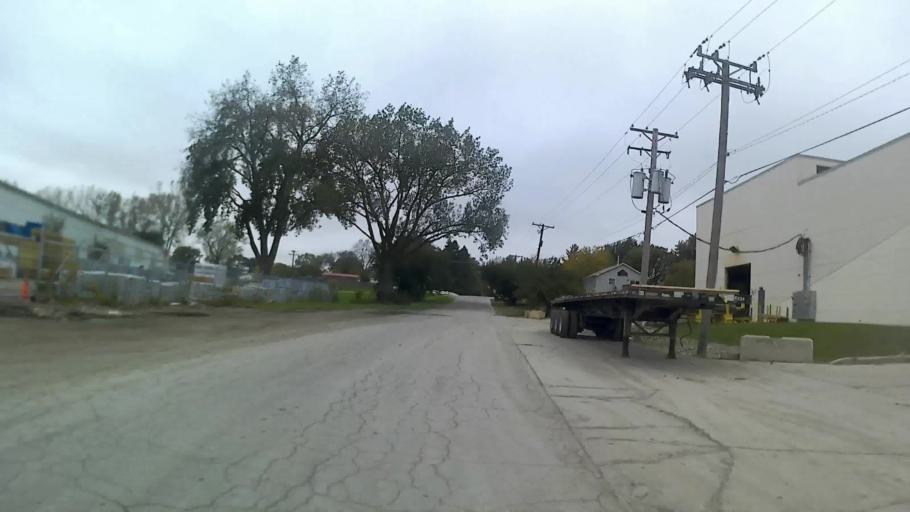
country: US
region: Illinois
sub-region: Kane County
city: Montgomery
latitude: 41.7475
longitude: -88.3400
